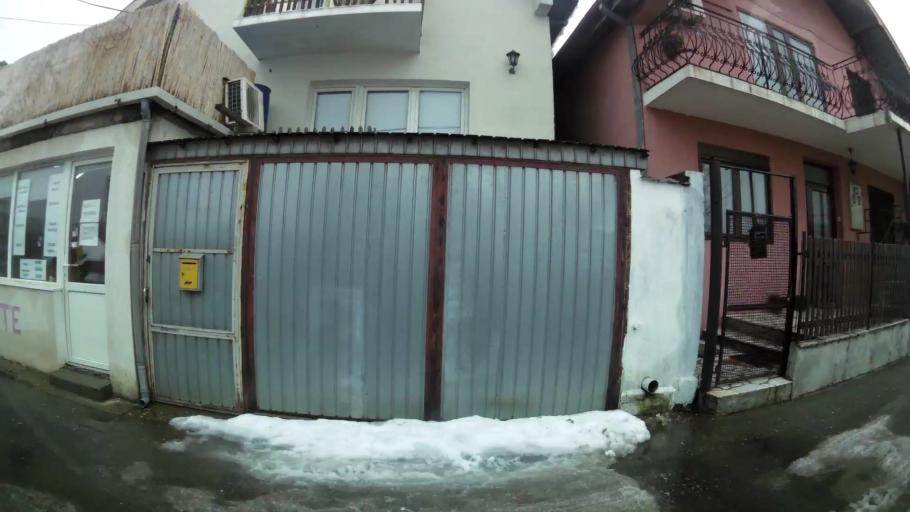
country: RS
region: Central Serbia
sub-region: Belgrade
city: Zvezdara
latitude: 44.7801
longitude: 20.5137
